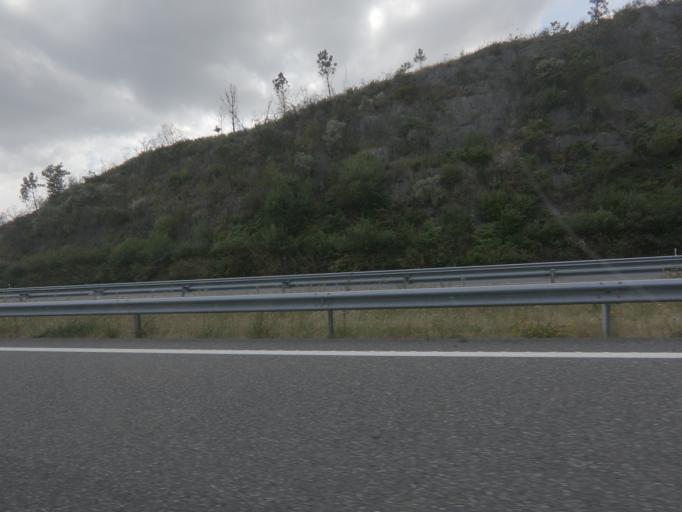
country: ES
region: Galicia
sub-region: Provincia de Ourense
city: Melon
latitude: 42.2804
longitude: -8.2027
